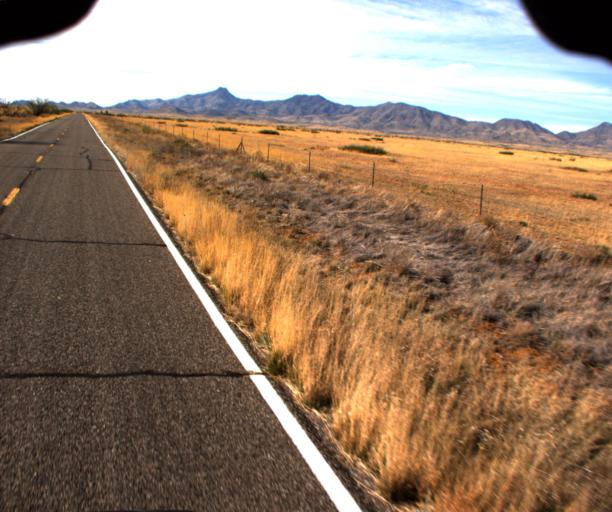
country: US
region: Arizona
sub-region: Cochise County
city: Willcox
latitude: 32.0854
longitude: -109.5261
